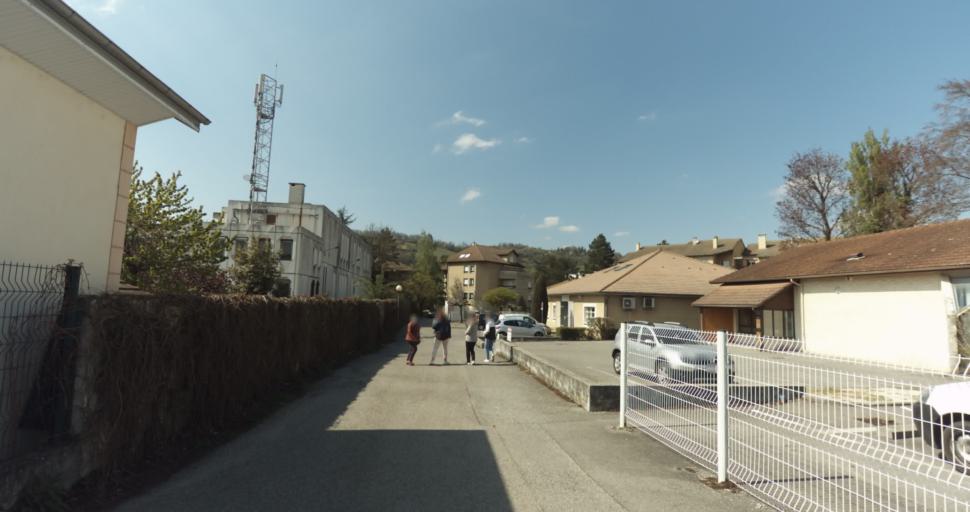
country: FR
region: Rhone-Alpes
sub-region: Departement de l'Isere
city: Saint-Marcellin
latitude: 45.1512
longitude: 5.3167
